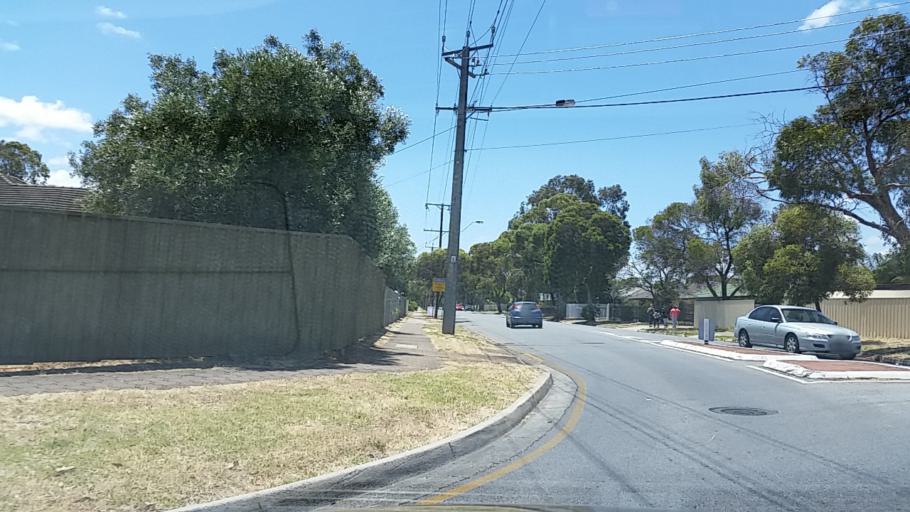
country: AU
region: South Australia
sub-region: Salisbury
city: Salisbury
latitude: -34.7659
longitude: 138.6260
